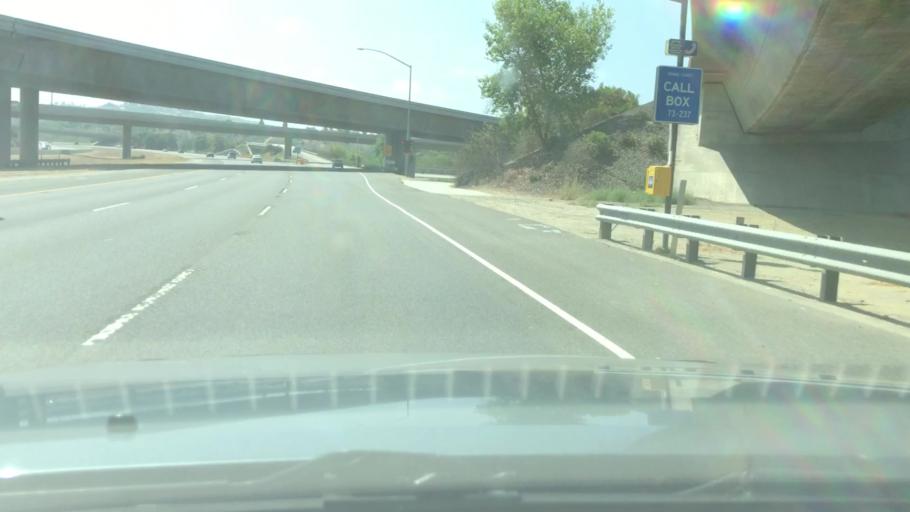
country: US
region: California
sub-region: Orange County
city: San Joaquin Hills
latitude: 33.6426
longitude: -117.8602
